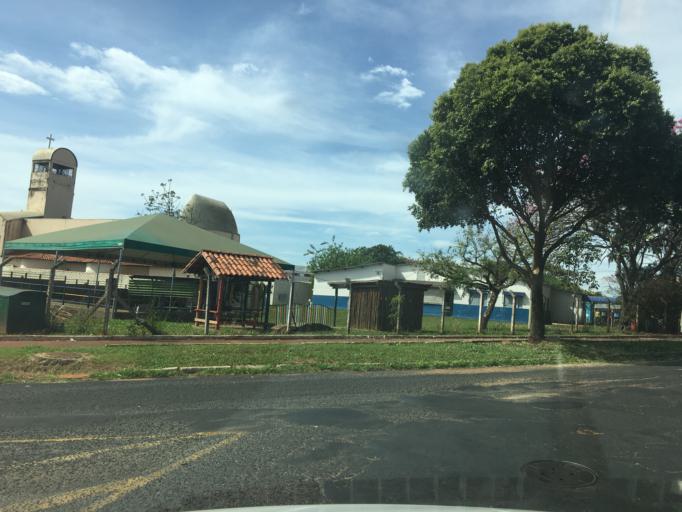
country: BR
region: Minas Gerais
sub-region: Uberlandia
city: Uberlandia
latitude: -18.9378
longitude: -48.3001
